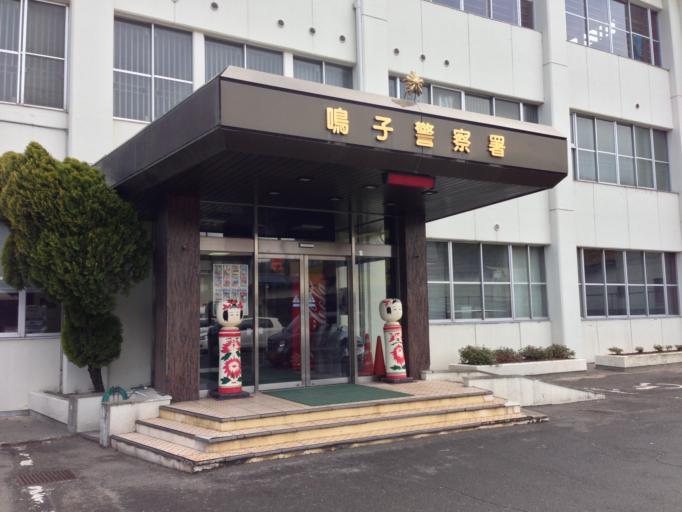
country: JP
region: Miyagi
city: Furukawa
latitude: 38.7485
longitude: 140.7265
